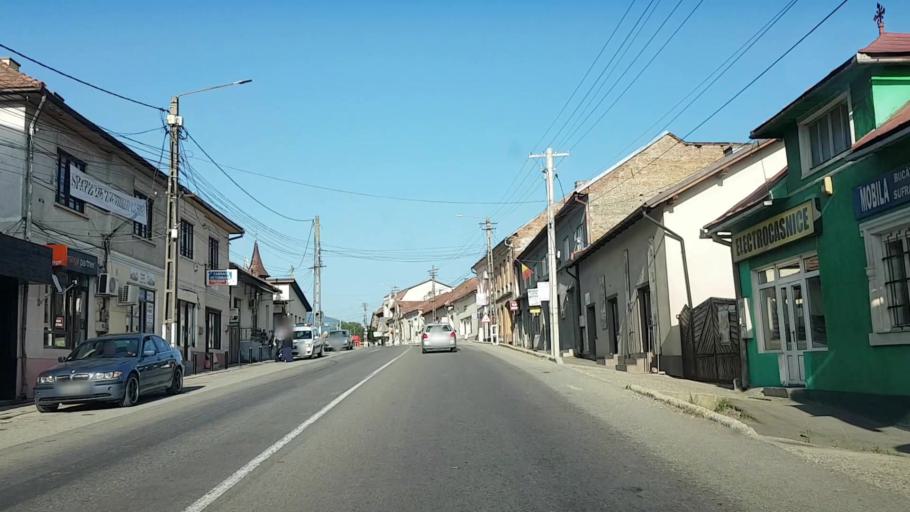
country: RO
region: Bistrita-Nasaud
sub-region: Comuna Bistrita Bargaului
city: Bistrita Bargaului
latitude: 47.2196
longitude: 24.7377
